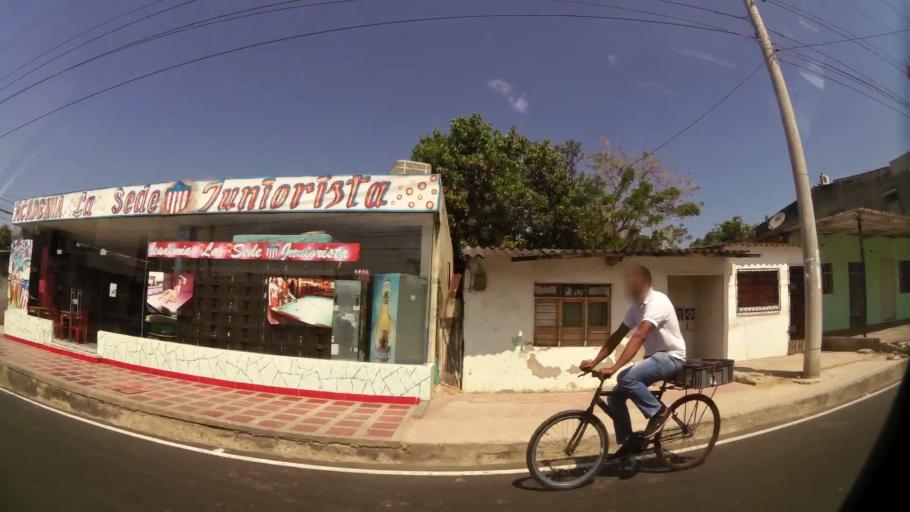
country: CO
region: Atlantico
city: Barranquilla
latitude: 10.9711
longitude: -74.8270
